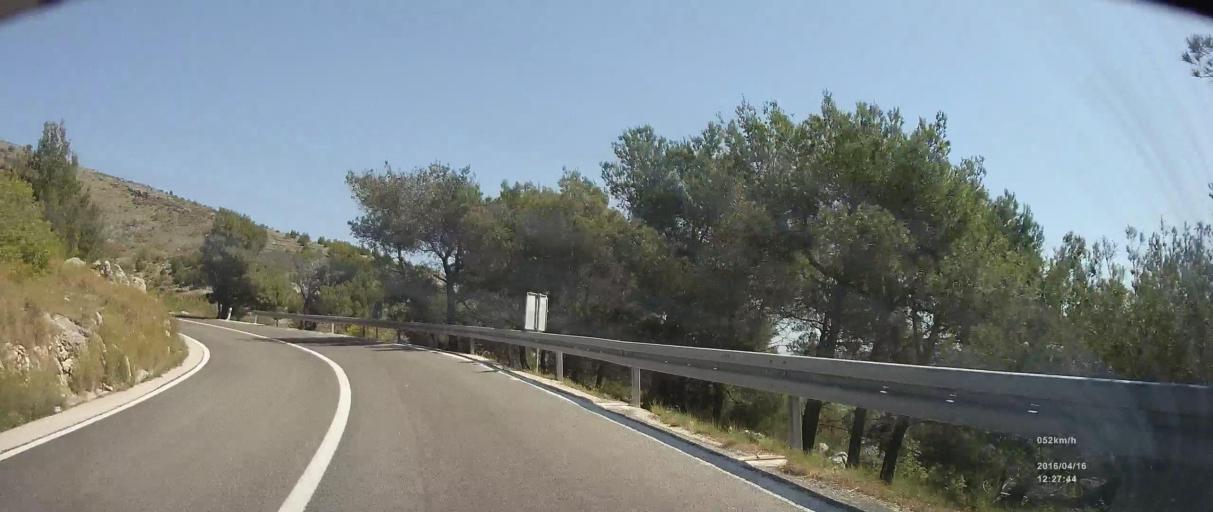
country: HR
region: Splitsko-Dalmatinska
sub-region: Grad Trogir
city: Trogir
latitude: 43.5189
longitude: 16.2054
